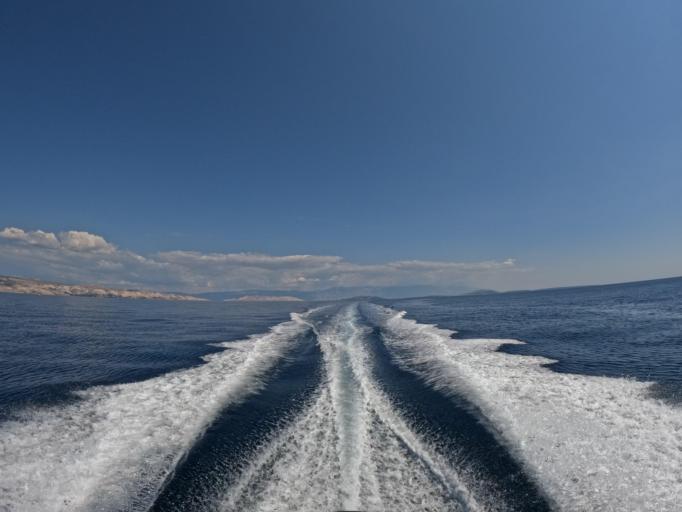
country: HR
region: Primorsko-Goranska
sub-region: Grad Krk
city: Krk
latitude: 44.9196
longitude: 14.5666
